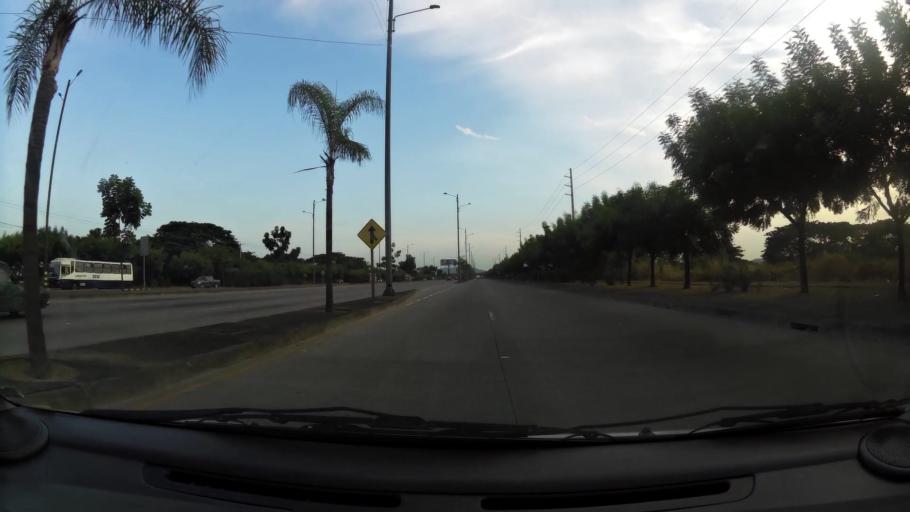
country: EC
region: Guayas
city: Eloy Alfaro
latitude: -2.1058
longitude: -79.8875
